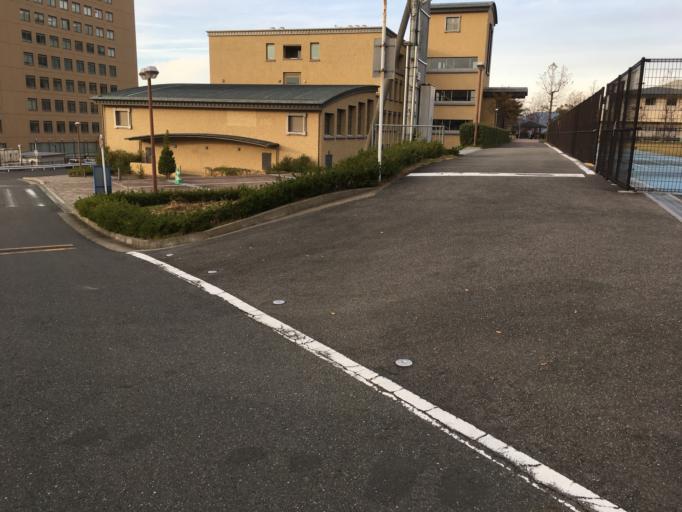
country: JP
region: Kyoto
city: Kameoka
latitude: 34.9936
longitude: 135.5525
